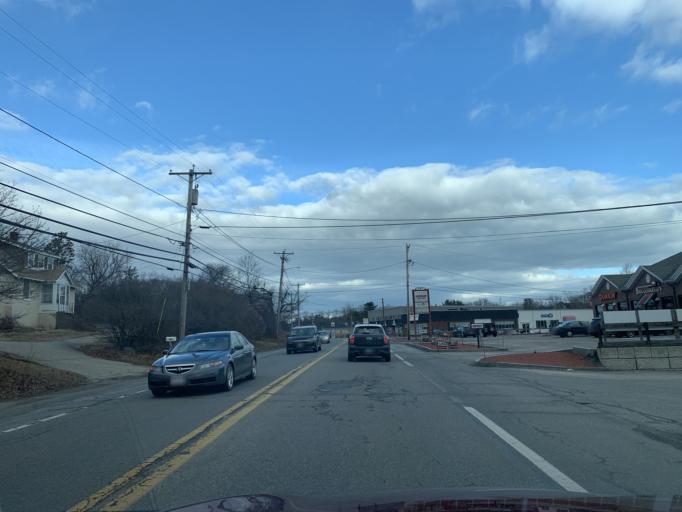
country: US
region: Massachusetts
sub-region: Essex County
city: Newburyport
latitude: 42.8206
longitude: -70.8679
